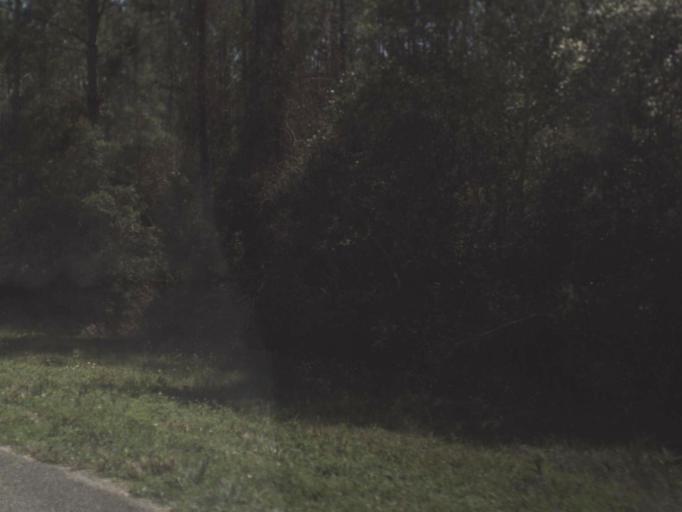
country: US
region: Florida
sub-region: Gulf County
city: Port Saint Joe
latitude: 29.7552
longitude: -85.2528
